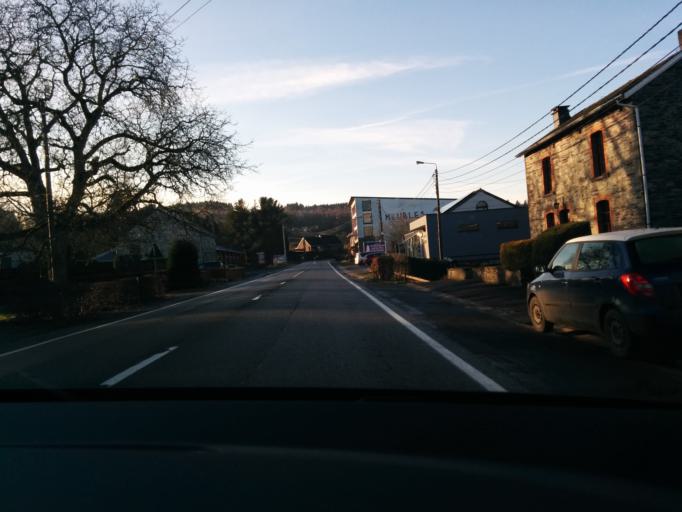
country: BE
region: Wallonia
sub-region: Province de Liege
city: Lierneux
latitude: 50.2542
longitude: 5.8138
